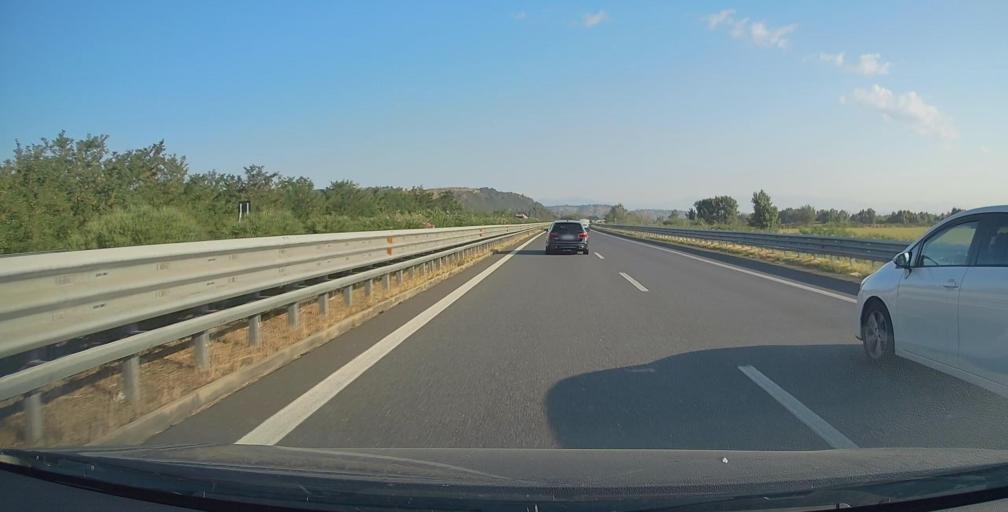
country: IT
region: Calabria
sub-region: Provincia di Cosenza
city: Taverna
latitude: 39.4735
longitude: 16.2157
